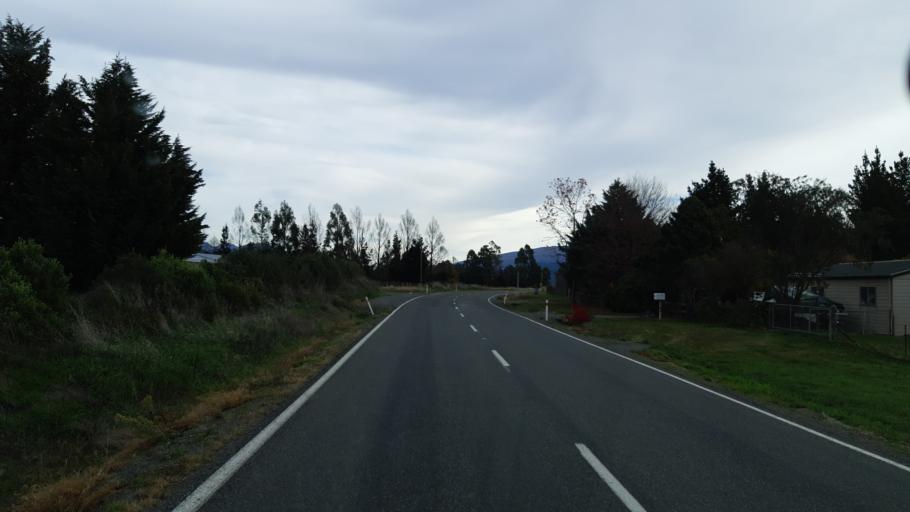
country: NZ
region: Tasman
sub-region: Tasman District
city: Brightwater
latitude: -41.6379
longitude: 173.3183
